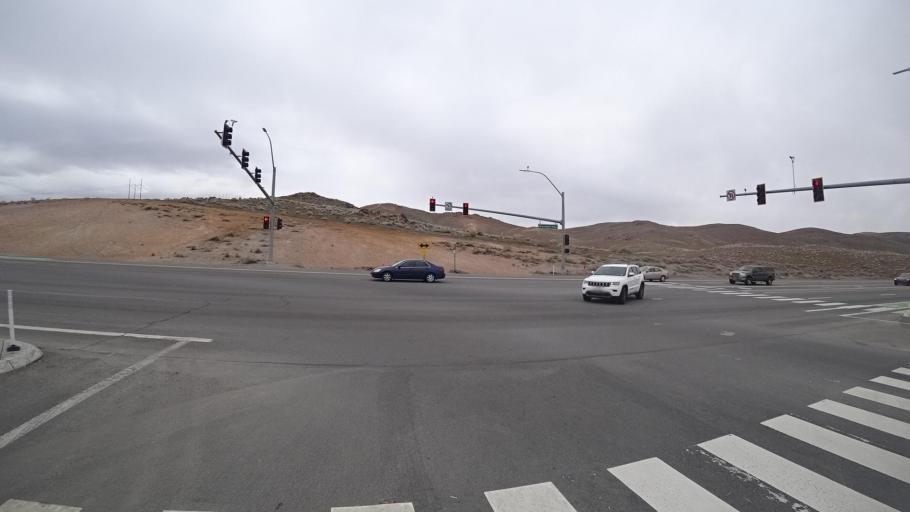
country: US
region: Nevada
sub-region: Washoe County
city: Sun Valley
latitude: 39.5765
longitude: -119.7456
